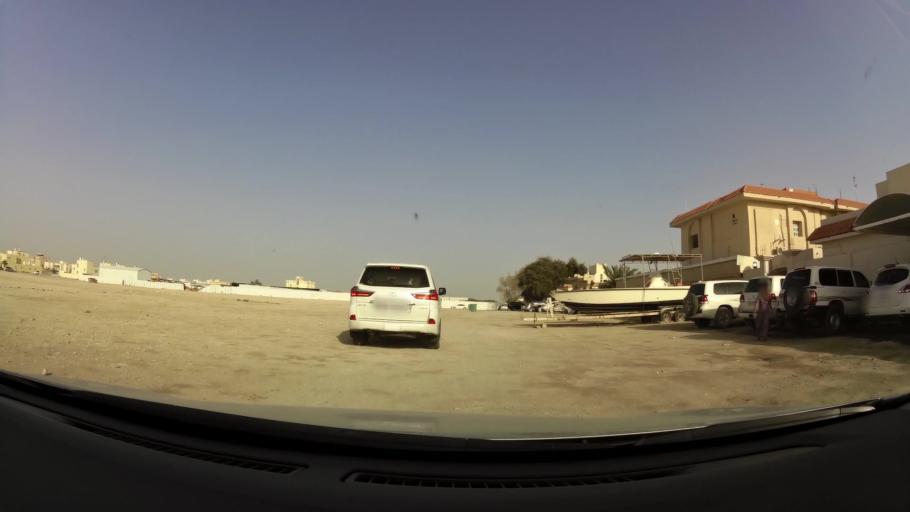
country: QA
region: Baladiyat ar Rayyan
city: Ar Rayyan
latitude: 25.3309
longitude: 51.4294
